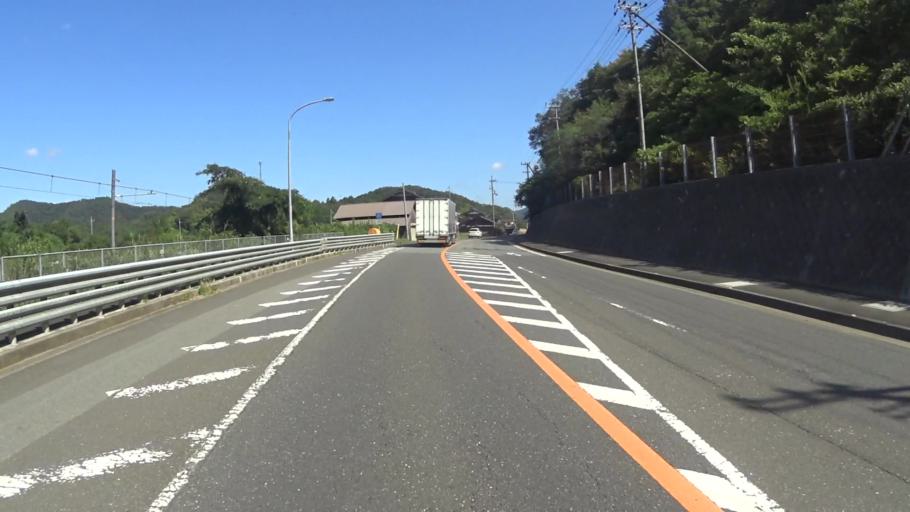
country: JP
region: Kyoto
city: Ayabe
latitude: 35.3525
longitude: 135.3108
